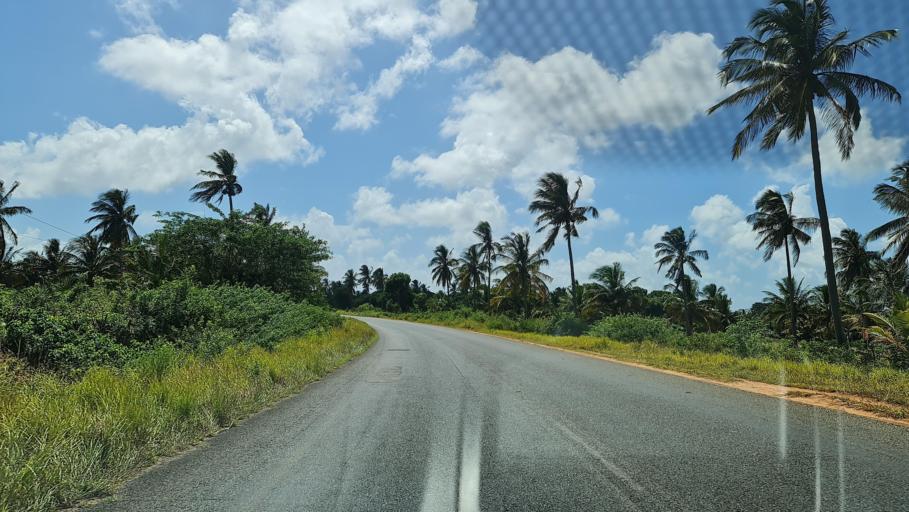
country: MZ
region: Inhambane
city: Maxixe
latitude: -24.5397
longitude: 34.9337
